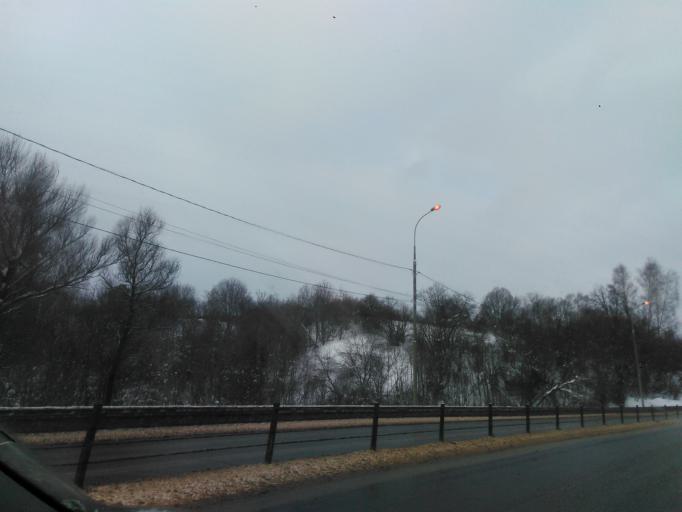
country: RU
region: Moskovskaya
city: Dedenevo
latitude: 56.2522
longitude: 37.5134
